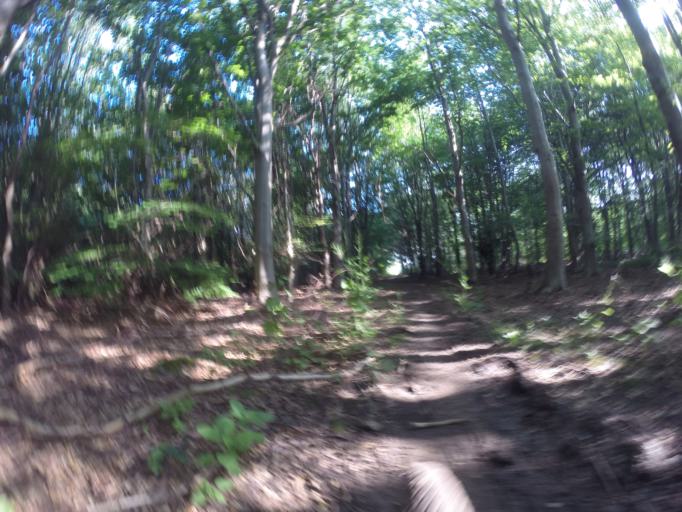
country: DK
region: Capital Region
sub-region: Ballerup Kommune
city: Ballerup
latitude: 55.6958
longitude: 12.3259
